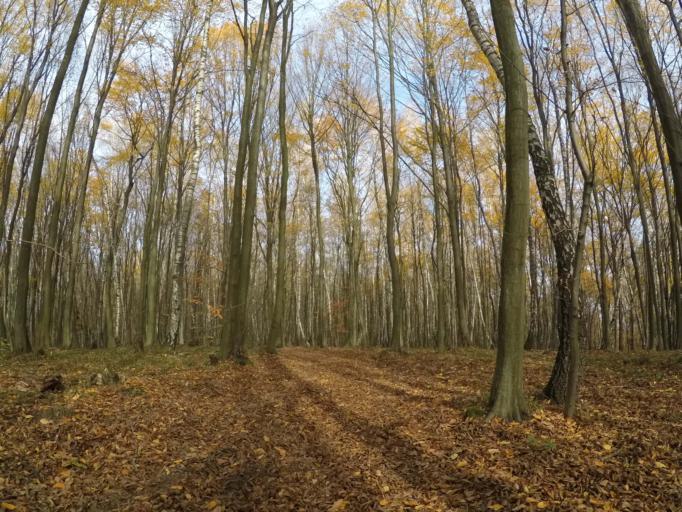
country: SK
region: Presovsky
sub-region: Okres Presov
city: Presov
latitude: 48.9244
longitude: 21.2202
